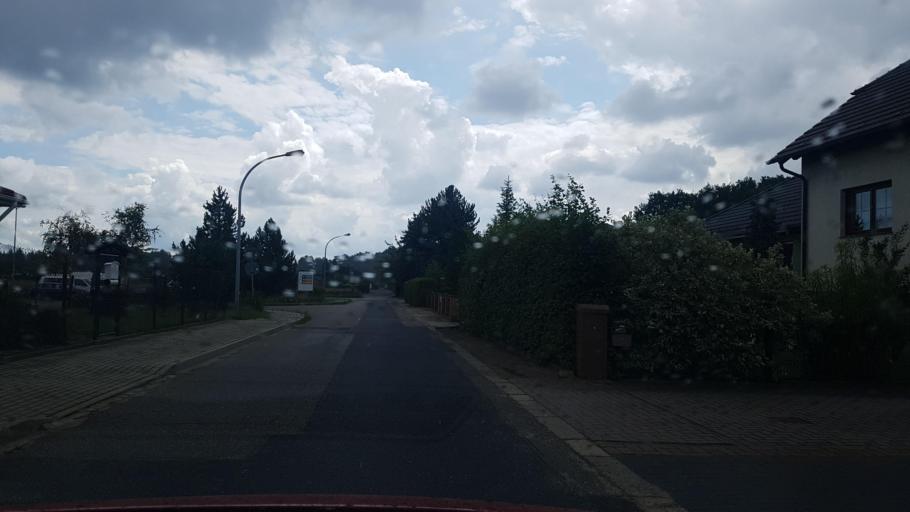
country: DE
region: Brandenburg
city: Herzberg
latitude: 51.6859
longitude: 13.2436
